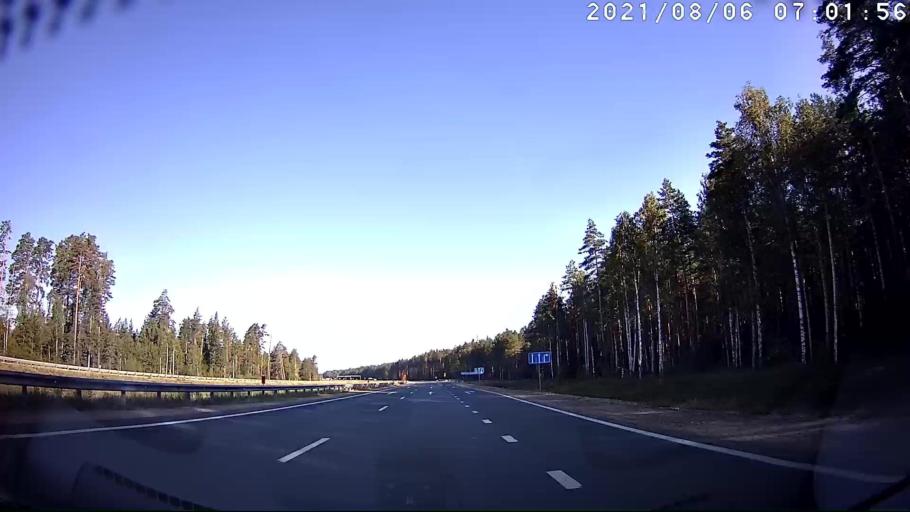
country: RU
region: Mariy-El
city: Surok
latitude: 56.5290
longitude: 48.0040
